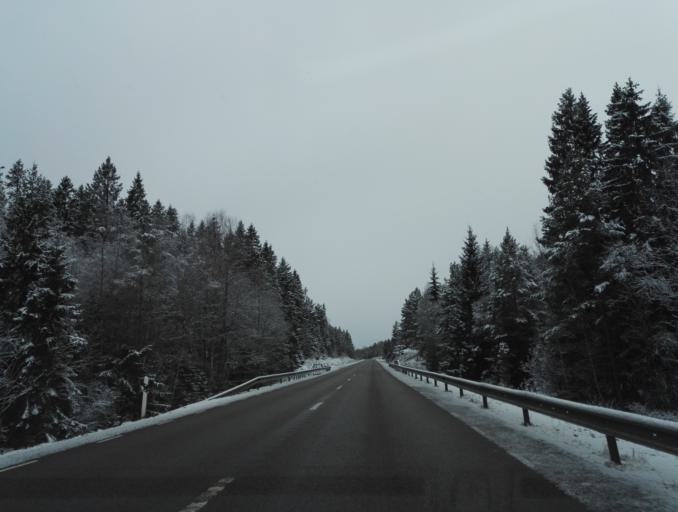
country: SE
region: Kronoberg
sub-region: Uppvidinge Kommun
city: Aseda
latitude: 57.1629
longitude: 15.4070
